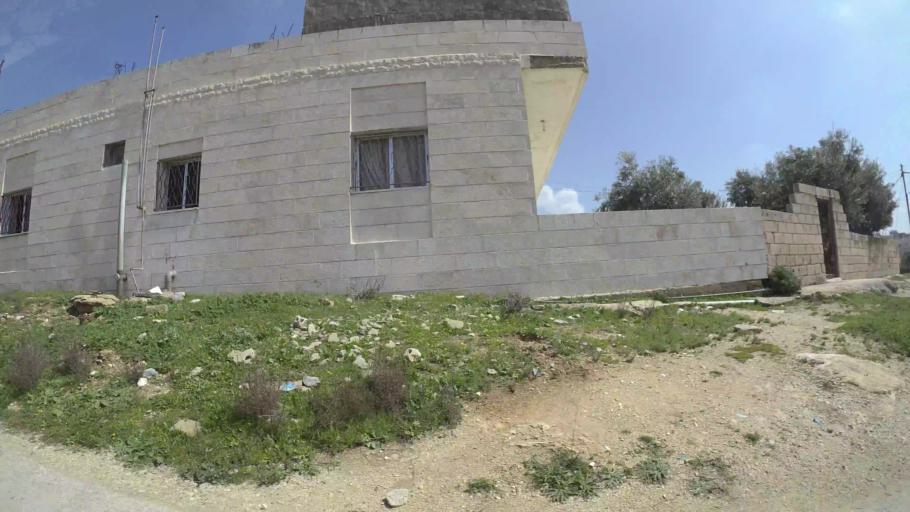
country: JO
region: Amman
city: Al Bunayyat ash Shamaliyah
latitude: 31.8933
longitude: 35.8890
